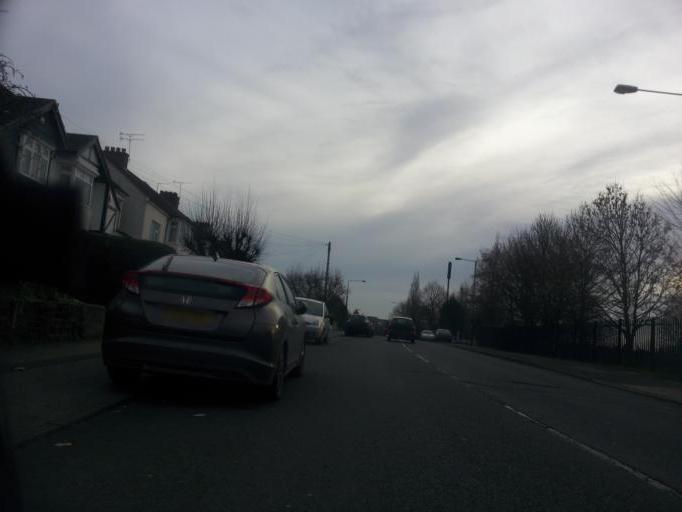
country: GB
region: England
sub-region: Kent
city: Gravesend
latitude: 51.4315
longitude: 0.3647
